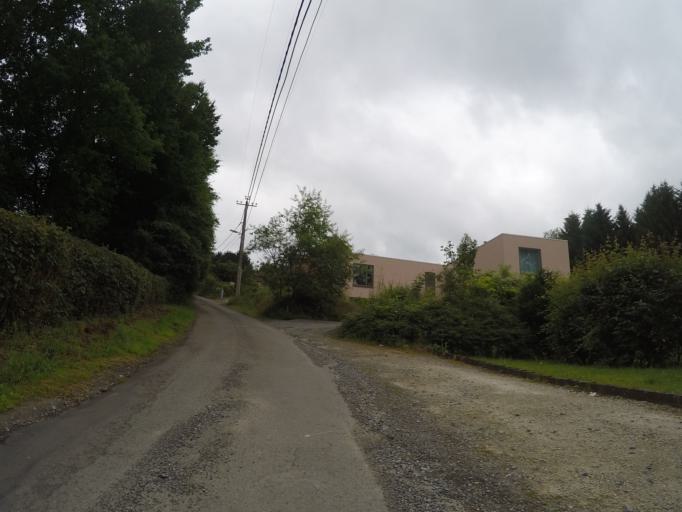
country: BE
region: Wallonia
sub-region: Province de Namur
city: Yvoir
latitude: 50.3316
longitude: 4.9278
